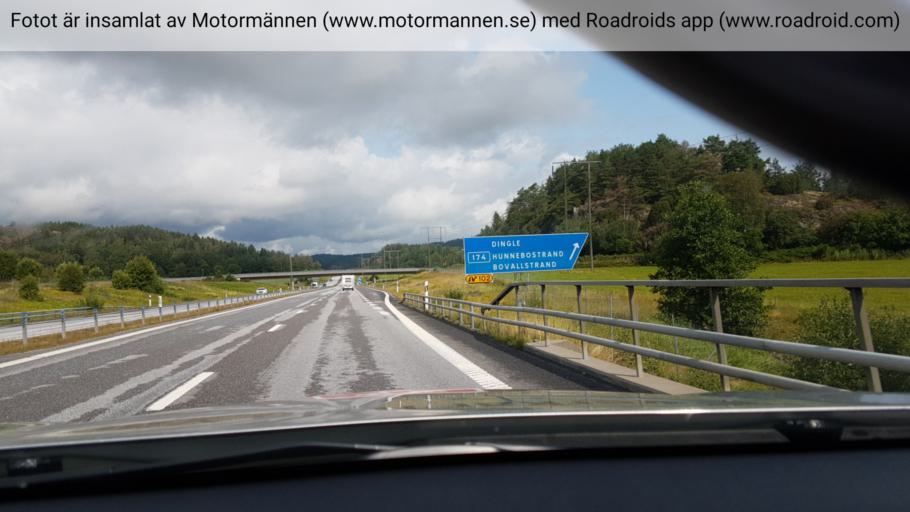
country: SE
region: Vaestra Goetaland
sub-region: Munkedals Kommun
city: Munkedal
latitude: 58.5180
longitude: 11.5505
